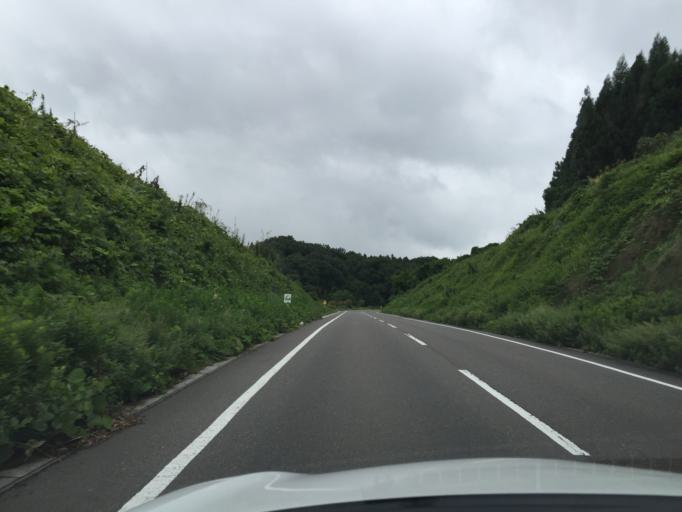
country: JP
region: Fukushima
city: Miharu
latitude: 37.4509
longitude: 140.5268
